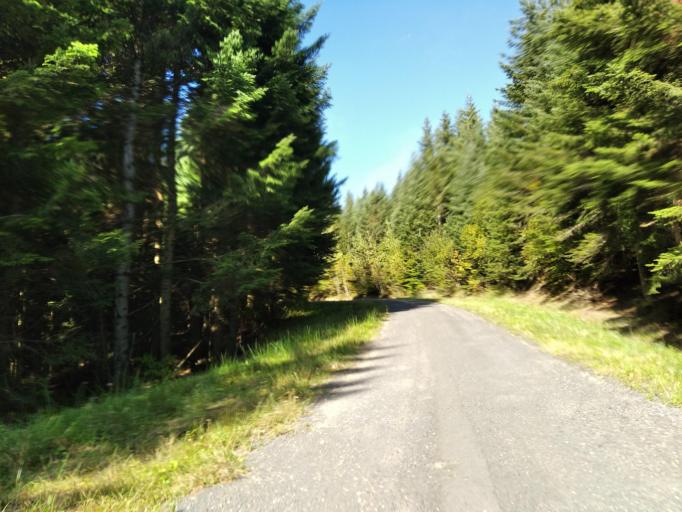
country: PL
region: Subcarpathian Voivodeship
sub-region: Powiat strzyzowski
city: Strzyzow
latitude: 49.8115
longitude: 21.8024
